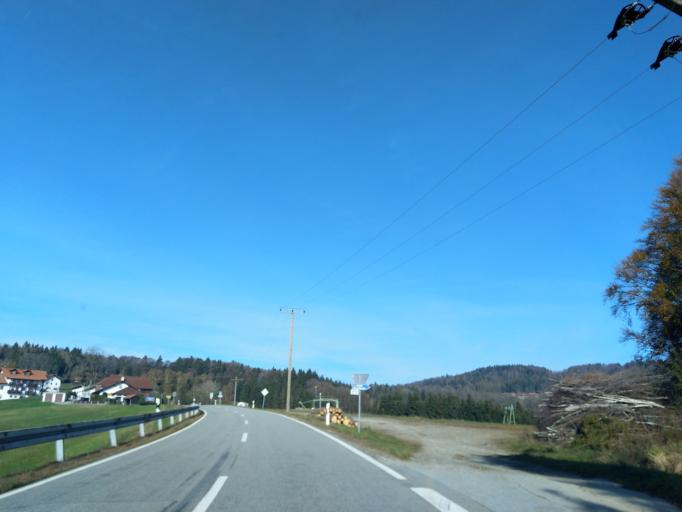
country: DE
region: Bavaria
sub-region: Lower Bavaria
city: Grattersdorf
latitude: 48.8061
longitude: 13.1911
